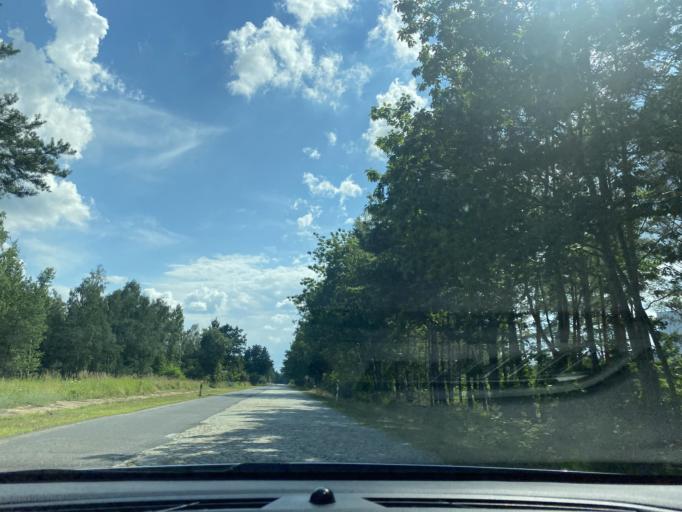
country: DE
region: Saxony
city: Boxberg
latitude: 51.4241
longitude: 14.5925
